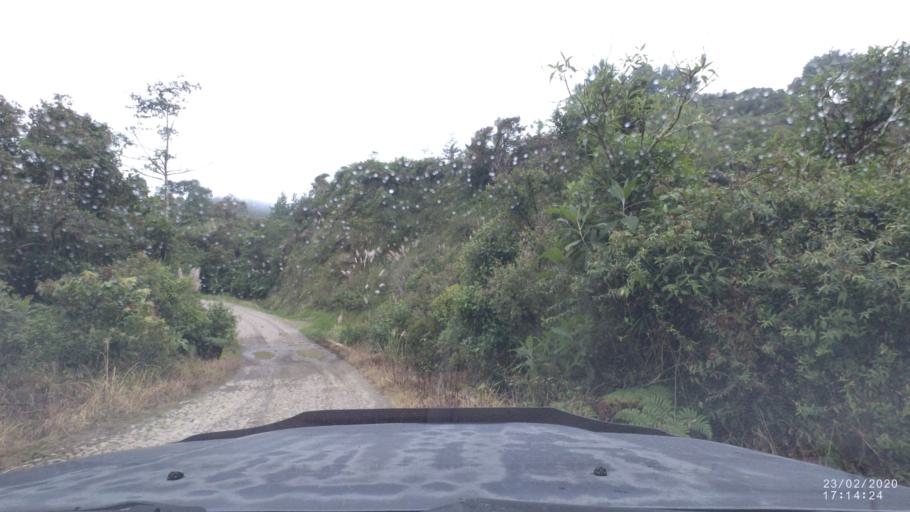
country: BO
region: Cochabamba
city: Colomi
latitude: -17.1373
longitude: -65.9430
